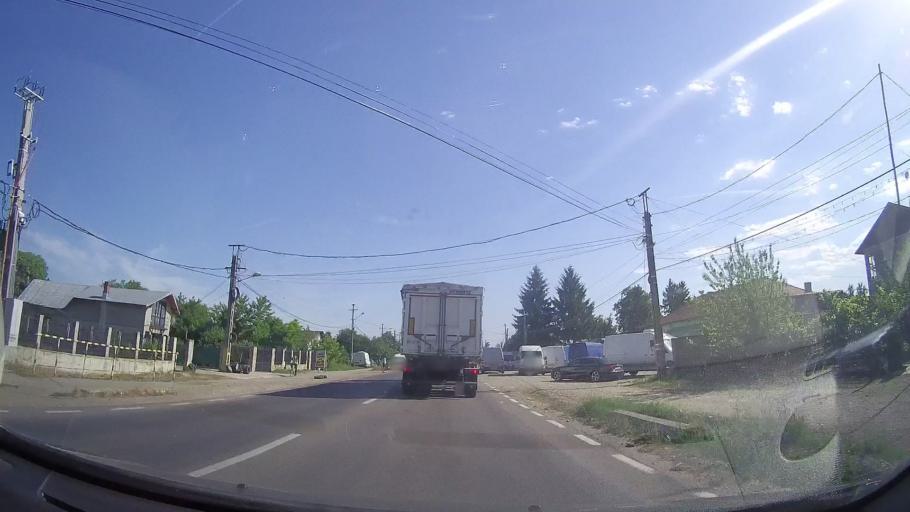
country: RO
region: Prahova
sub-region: Comuna Lipanesti
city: Lipanesti
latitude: 45.0495
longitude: 26.0193
